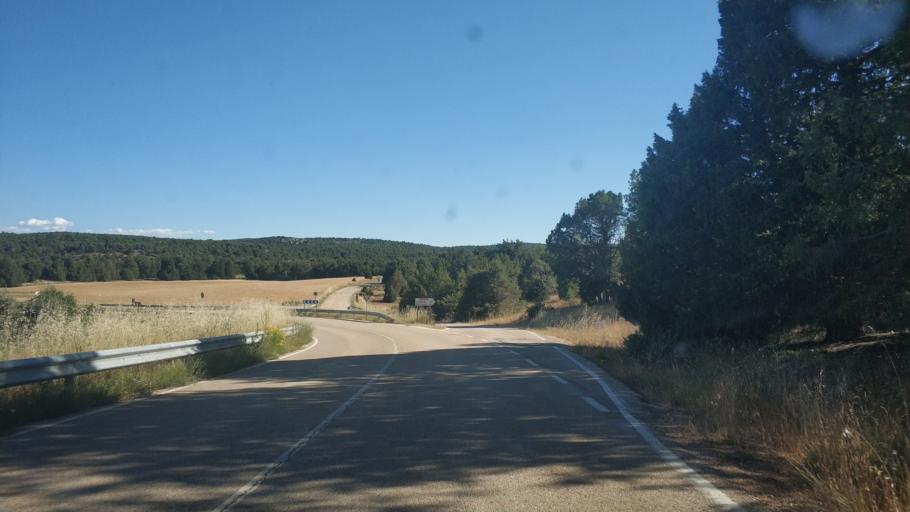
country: ES
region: Castille and Leon
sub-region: Provincia de Soria
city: Liceras
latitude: 41.4398
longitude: -3.2143
